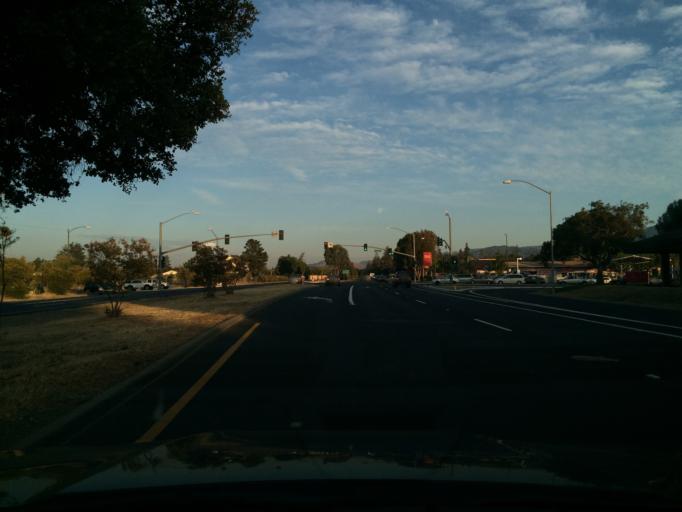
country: US
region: California
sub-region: Santa Clara County
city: Seven Trees
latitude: 37.2222
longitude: -121.8632
